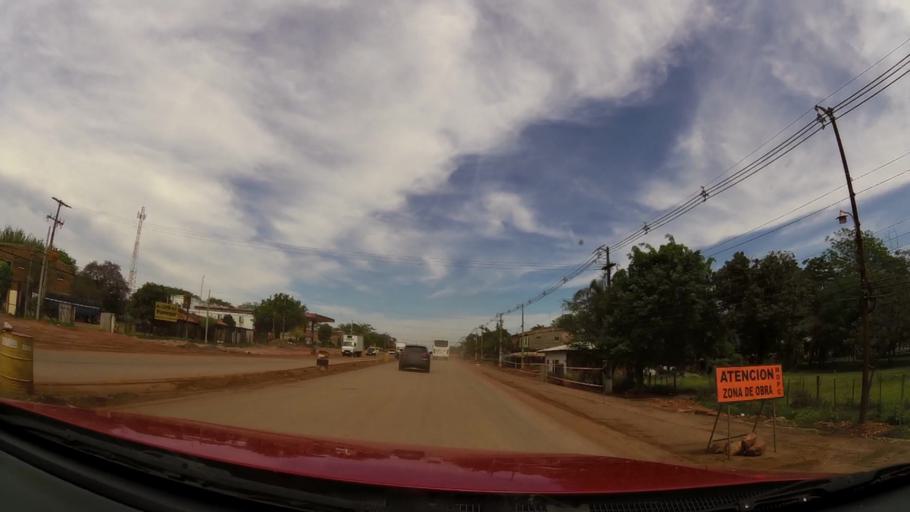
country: PY
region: Central
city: Limpio
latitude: -25.1967
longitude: -57.5141
